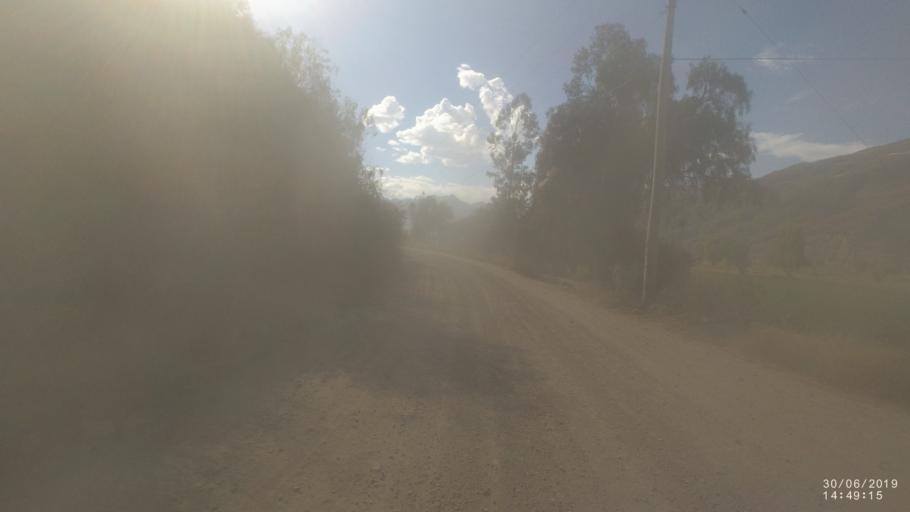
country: BO
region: Cochabamba
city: Irpa Irpa
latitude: -17.7844
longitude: -66.3413
